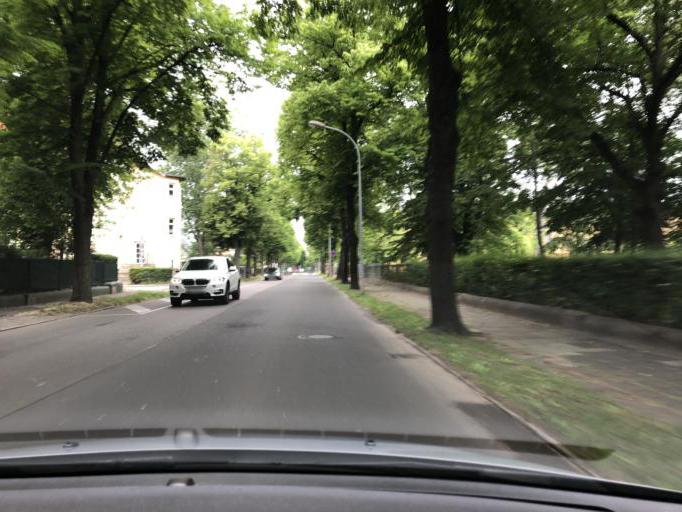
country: DE
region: Saxony-Anhalt
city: Weissenfels
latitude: 51.1997
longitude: 11.9914
